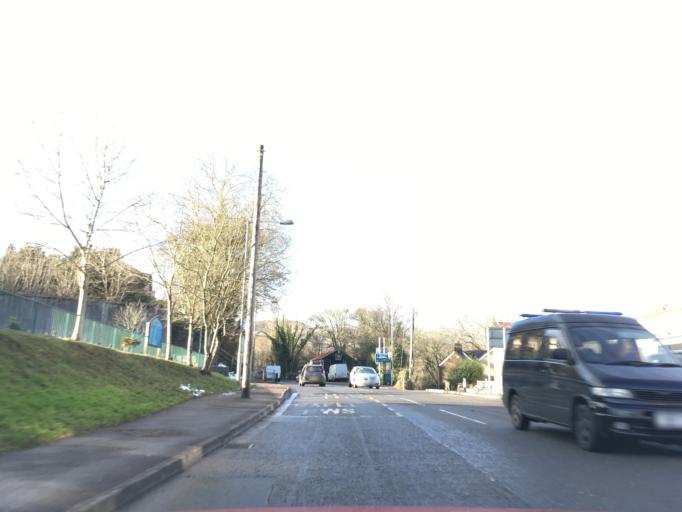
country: GB
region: Wales
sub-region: Torfaen County Borough
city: Pontypool
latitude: 51.6987
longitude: -3.0322
